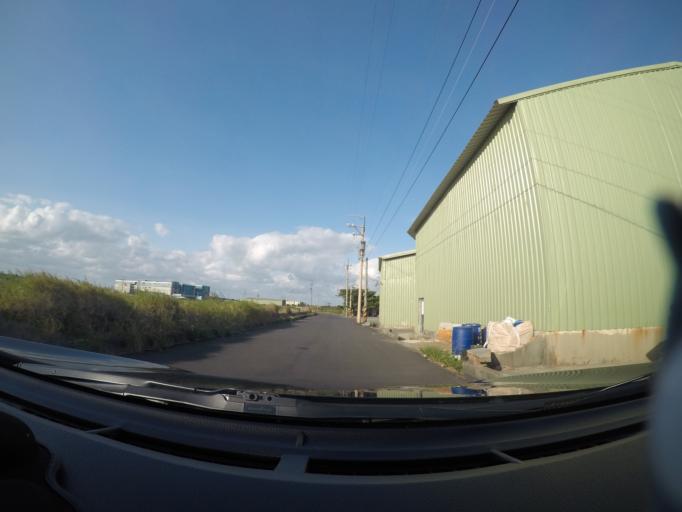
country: TW
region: Taiwan
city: Taoyuan City
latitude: 25.1035
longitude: 121.2522
